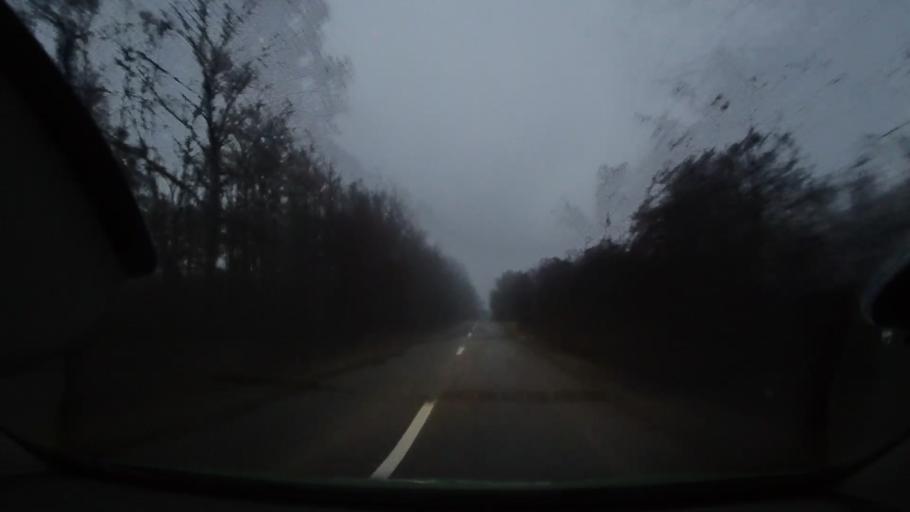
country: RO
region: Arad
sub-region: Comuna Beliu
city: Beliu
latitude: 46.4842
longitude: 22.0058
